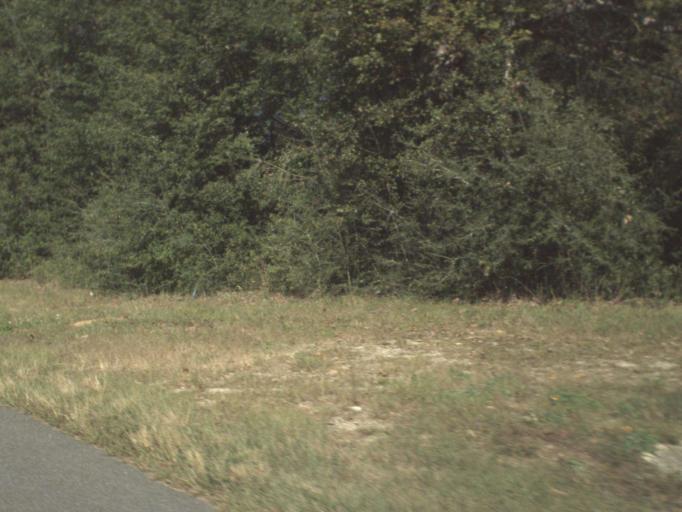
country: US
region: Florida
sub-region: Okaloosa County
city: Crestview
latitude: 30.8880
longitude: -86.5068
